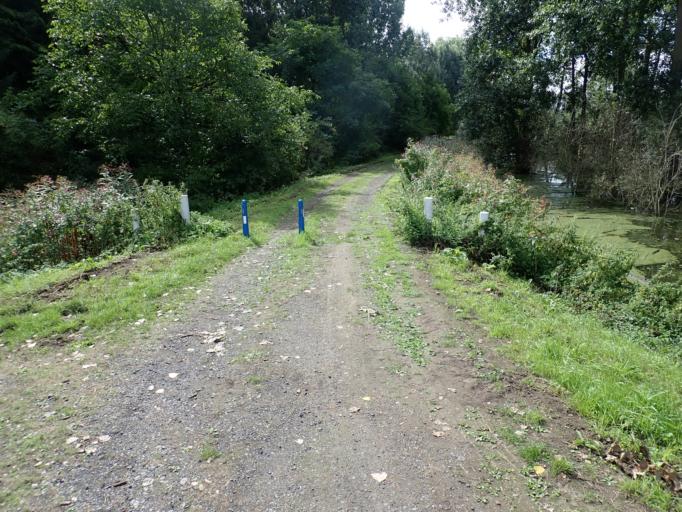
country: BE
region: Flanders
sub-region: Provincie Oost-Vlaanderen
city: Hamme
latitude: 51.1063
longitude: 4.1304
